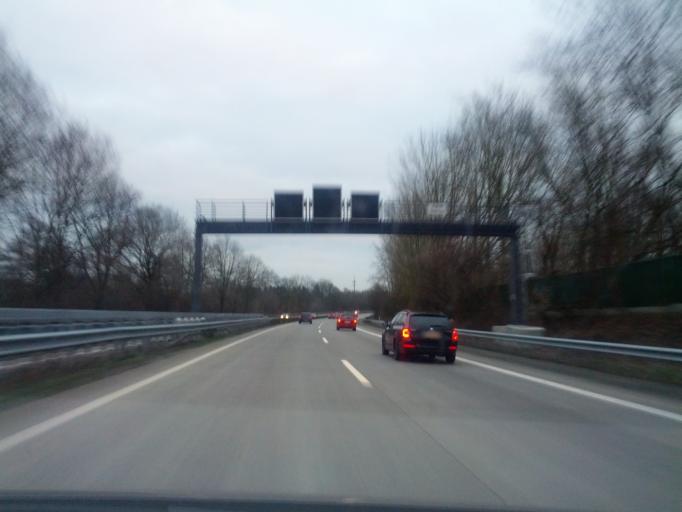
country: DE
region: Lower Saxony
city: Lilienthal
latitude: 53.0781
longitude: 8.9487
